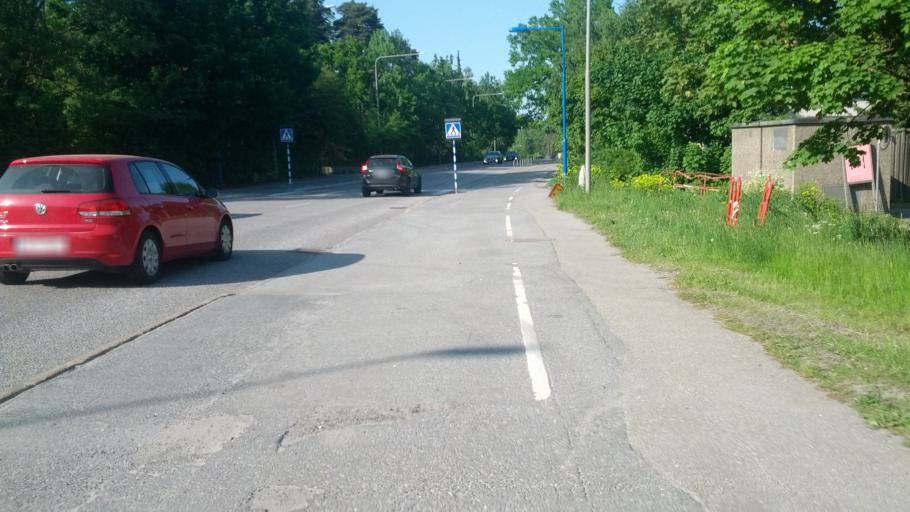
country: SE
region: Stockholm
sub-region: Danderyds Kommun
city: Djursholm
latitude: 59.3963
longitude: 18.0522
